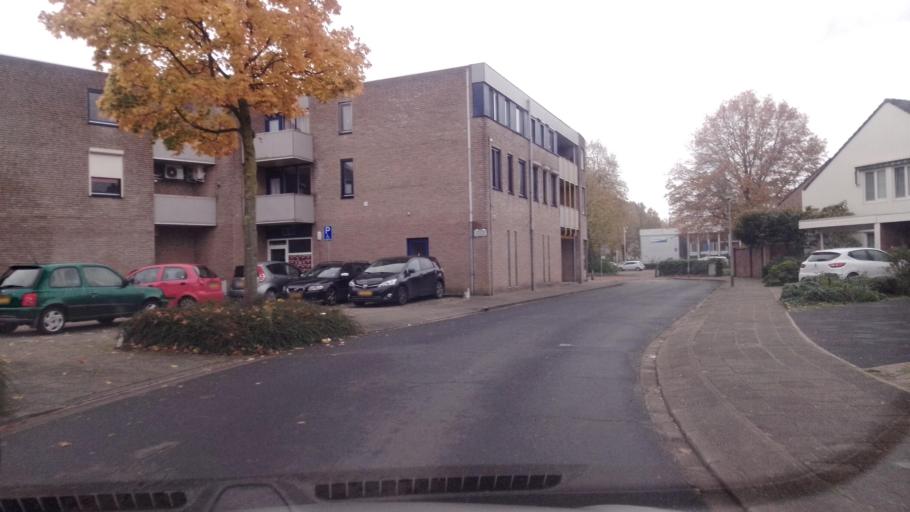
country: NL
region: Limburg
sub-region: Gemeente Peel en Maas
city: Maasbree
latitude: 51.4559
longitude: 6.0501
